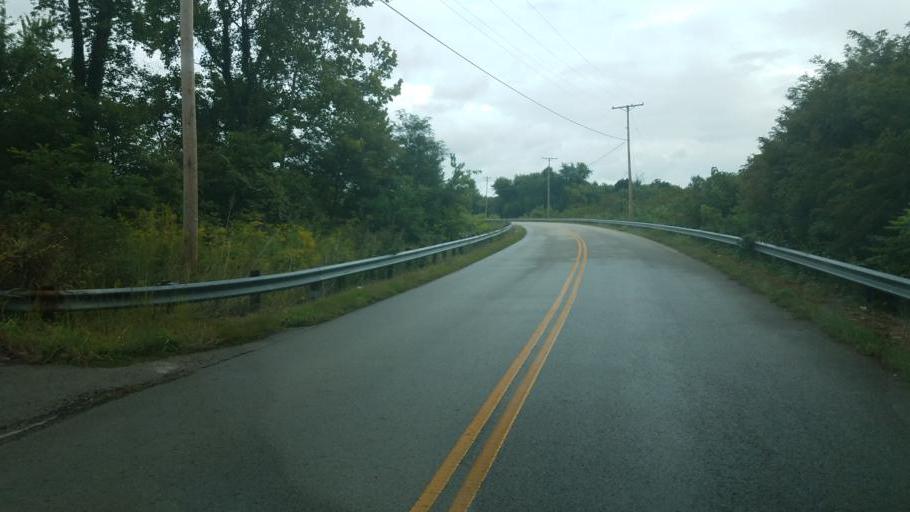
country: US
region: Ohio
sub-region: Scioto County
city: Wheelersburg
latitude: 38.7135
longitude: -82.8680
